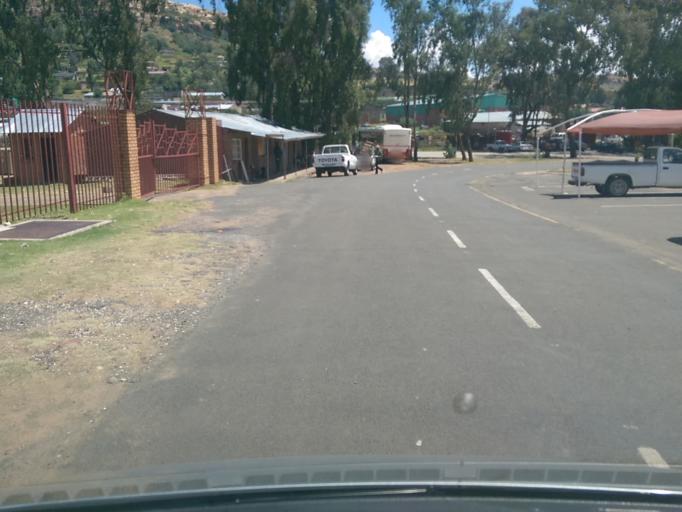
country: LS
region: Maseru
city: Nako
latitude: -29.4519
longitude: 27.7227
